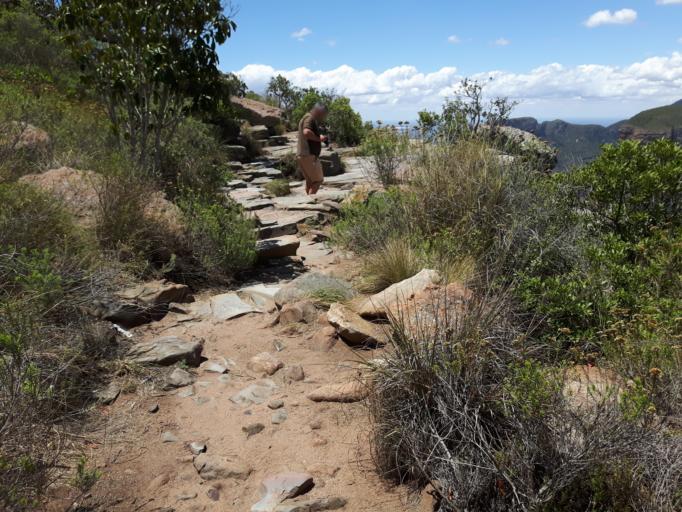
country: ZA
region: Limpopo
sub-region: Mopani District Municipality
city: Hoedspruit
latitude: -24.5733
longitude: 30.7991
